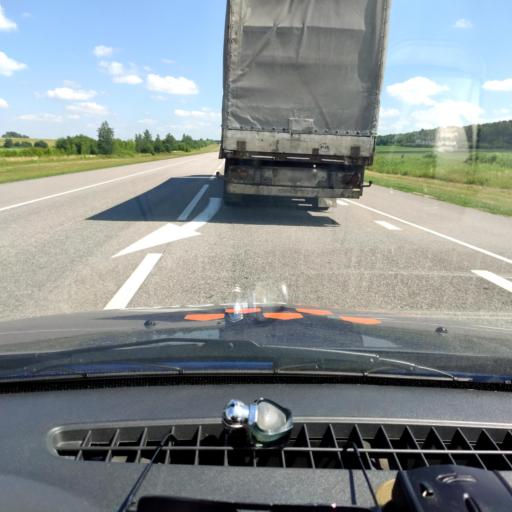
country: RU
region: Orjol
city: Orel
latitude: 52.8562
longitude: 36.2145
